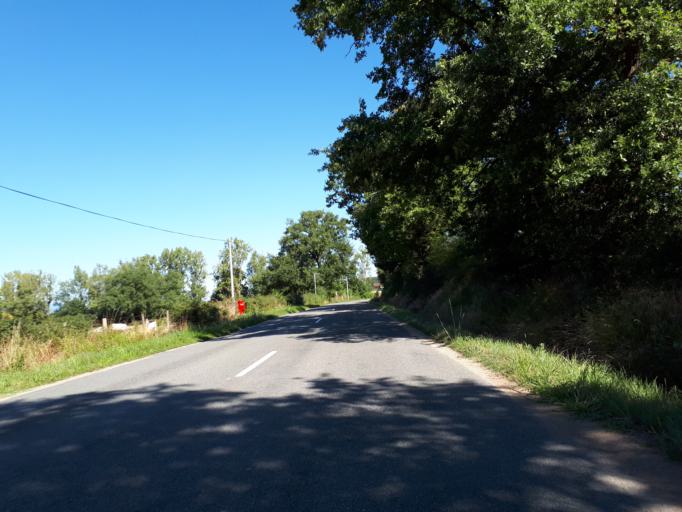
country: FR
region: Rhone-Alpes
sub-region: Departement de la Loire
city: Civens
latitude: 45.7872
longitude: 4.2418
